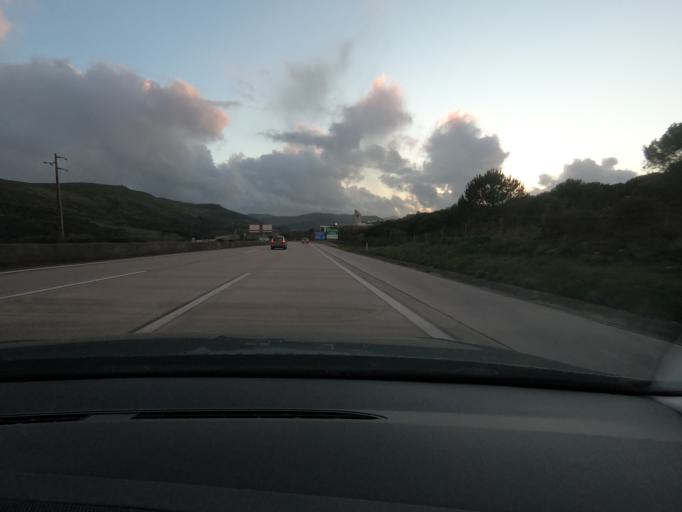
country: PT
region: Lisbon
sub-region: Loures
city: Bucelas
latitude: 38.9068
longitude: -9.0856
